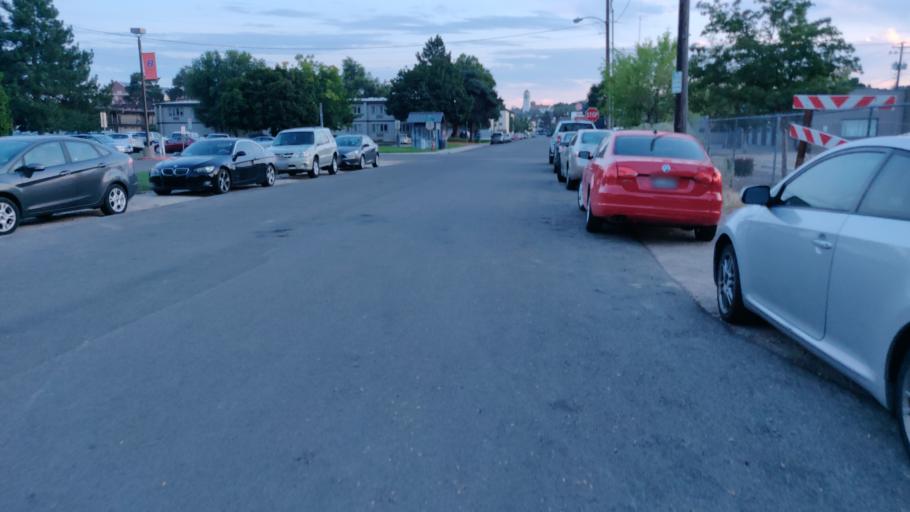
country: US
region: Idaho
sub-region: Ada County
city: Boise
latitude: 43.6093
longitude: -116.2113
